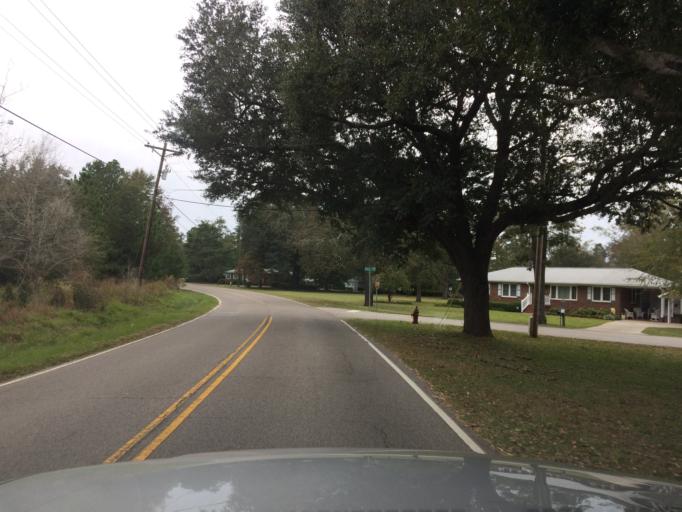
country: US
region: South Carolina
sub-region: Aiken County
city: New Ellenton
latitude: 33.4200
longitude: -81.6932
